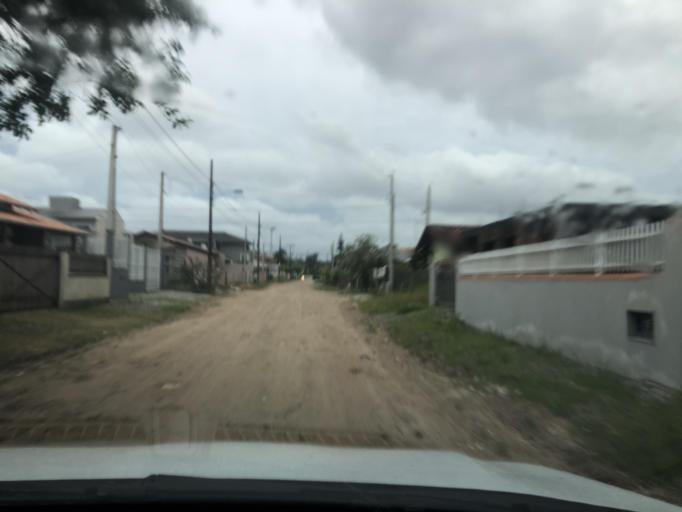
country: BR
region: Santa Catarina
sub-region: Sao Francisco Do Sul
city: Sao Francisco do Sul
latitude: -26.2216
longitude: -48.5269
